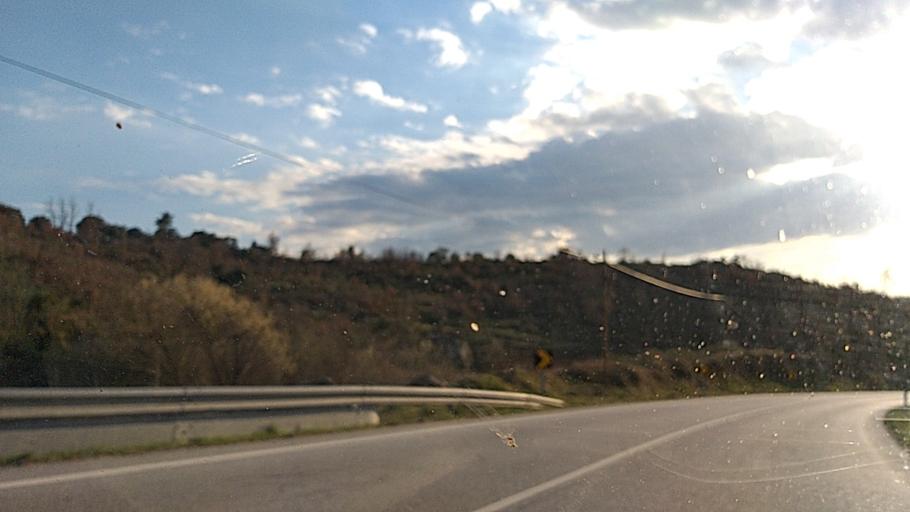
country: ES
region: Castille and Leon
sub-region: Provincia de Salamanca
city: Aldea del Obispo
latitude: 40.7061
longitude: -6.9190
